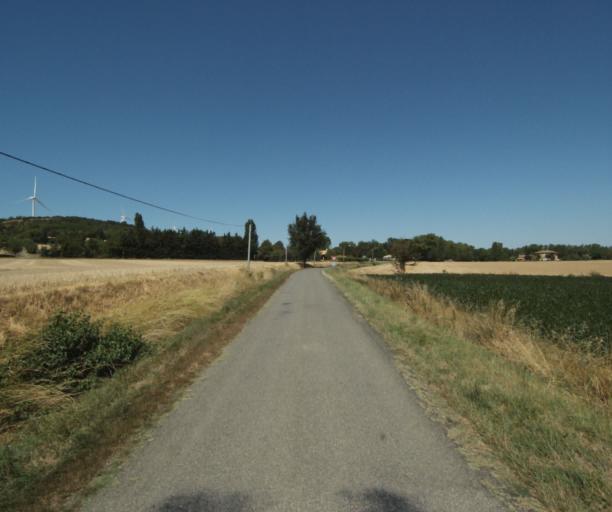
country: FR
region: Midi-Pyrenees
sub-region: Departement de la Haute-Garonne
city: Saint-Felix-Lauragais
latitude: 43.4582
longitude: 1.9287
